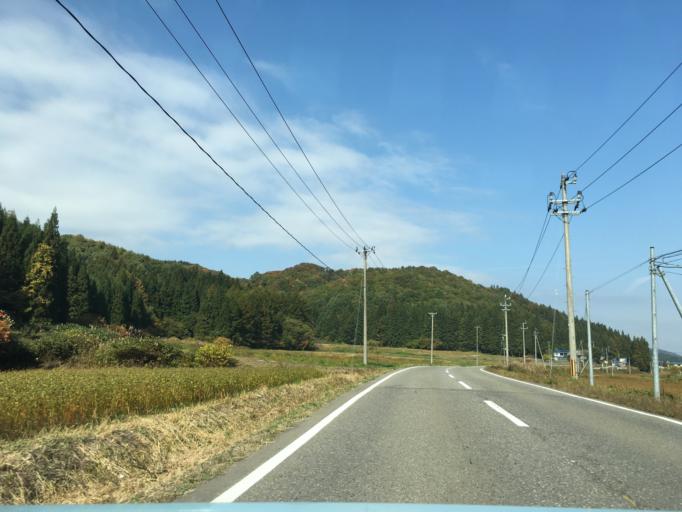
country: JP
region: Fukushima
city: Inawashiro
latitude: 37.4310
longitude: 140.0240
